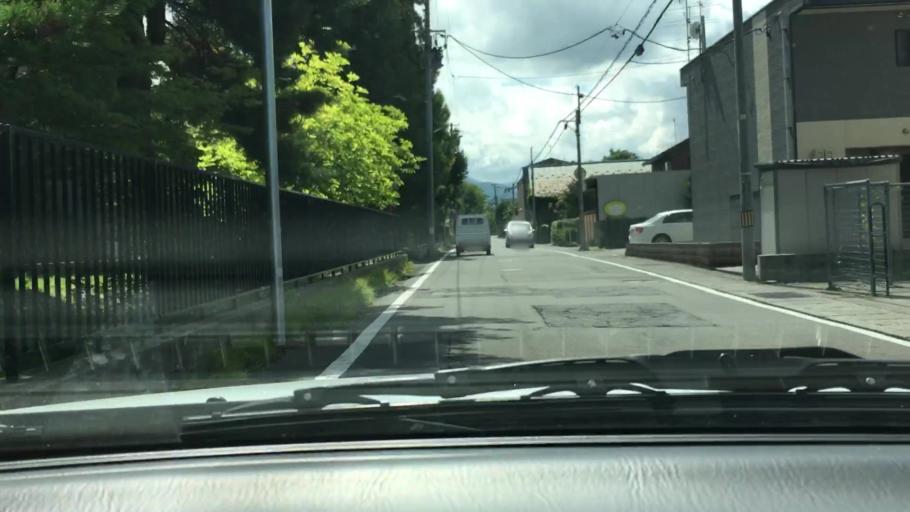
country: JP
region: Aomori
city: Hirosaki
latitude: 40.5903
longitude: 140.4709
